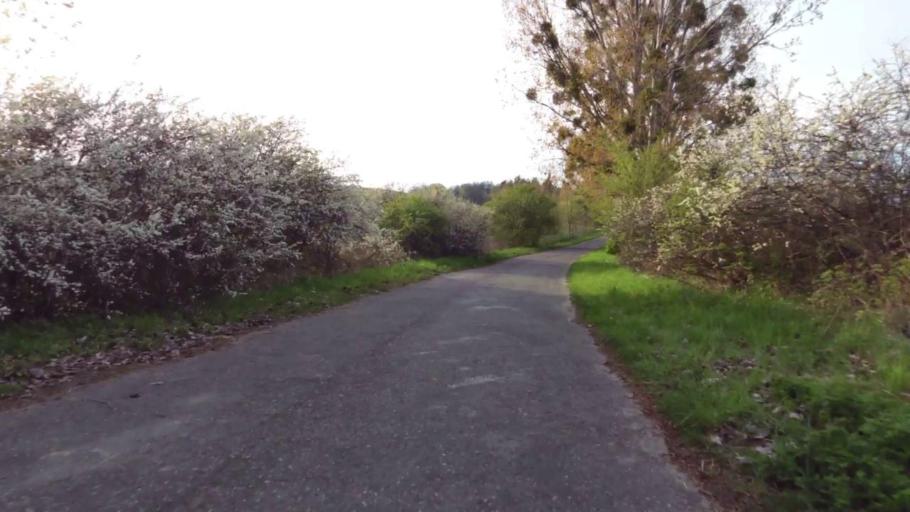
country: PL
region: West Pomeranian Voivodeship
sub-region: Powiat mysliborski
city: Mysliborz
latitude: 52.8957
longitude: 14.7754
